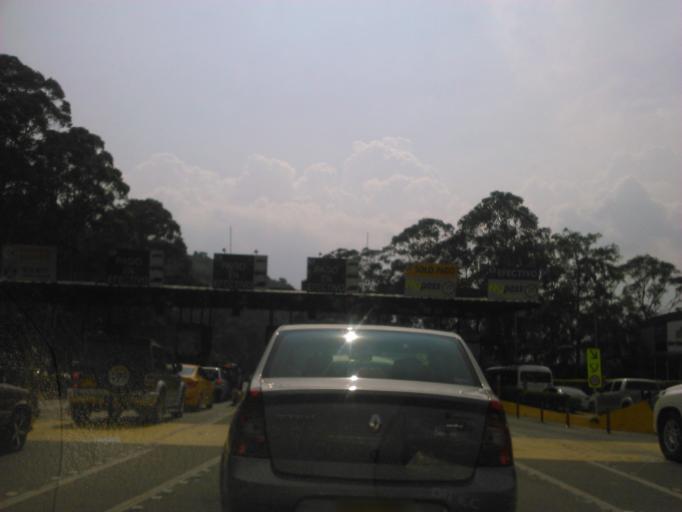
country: CO
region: Antioquia
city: Municipio de Copacabana
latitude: 6.3280
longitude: -75.5151
